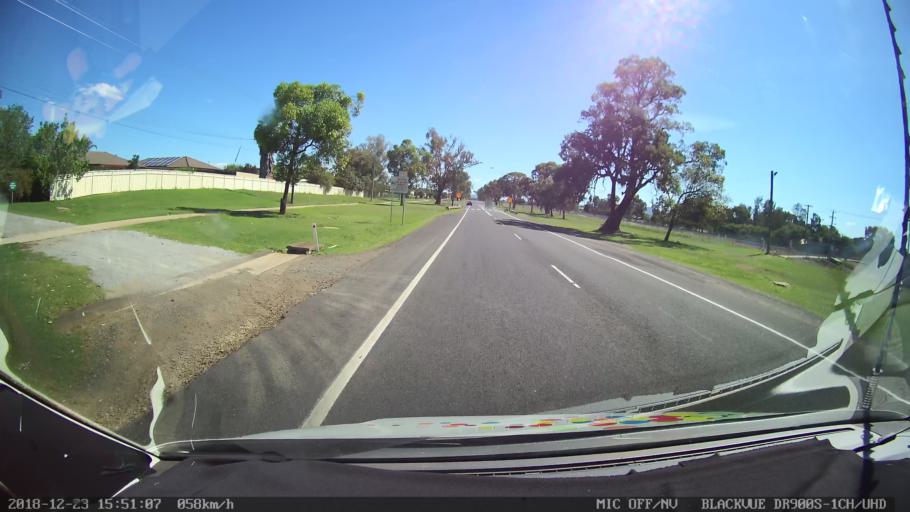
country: AU
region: New South Wales
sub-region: Tamworth Municipality
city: South Tamworth
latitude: -31.1102
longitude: 150.8978
